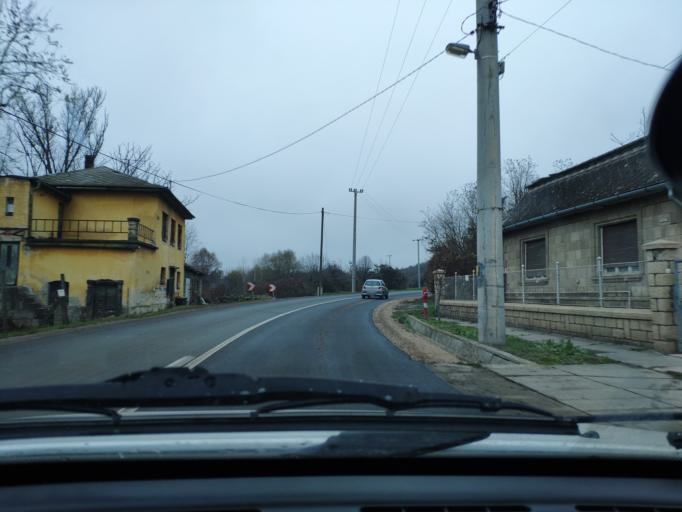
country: HU
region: Pest
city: Soskut
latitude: 47.4107
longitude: 18.8307
